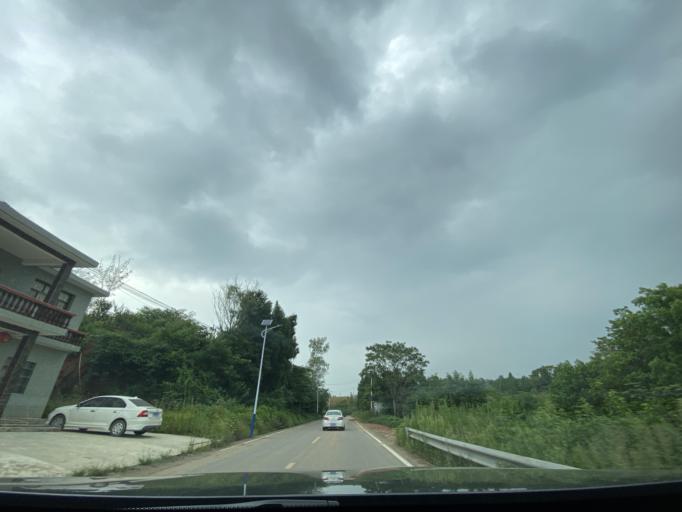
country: CN
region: Sichuan
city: Jiancheng
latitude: 30.5493
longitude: 104.5236
